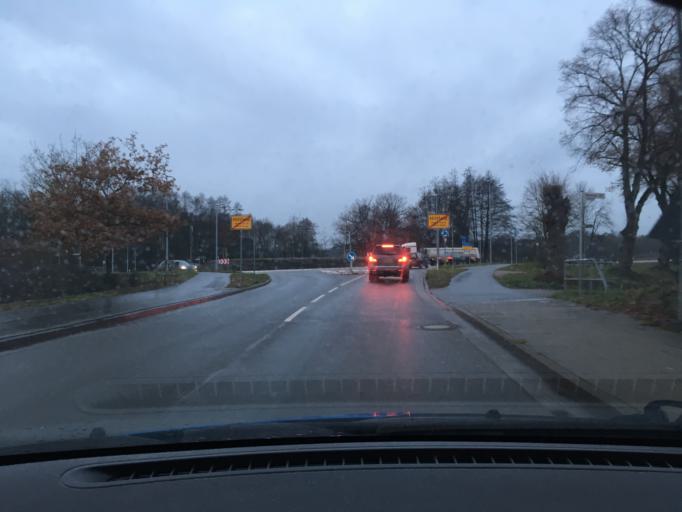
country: DE
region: Lower Saxony
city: Seevetal
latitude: 53.3872
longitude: 9.9751
